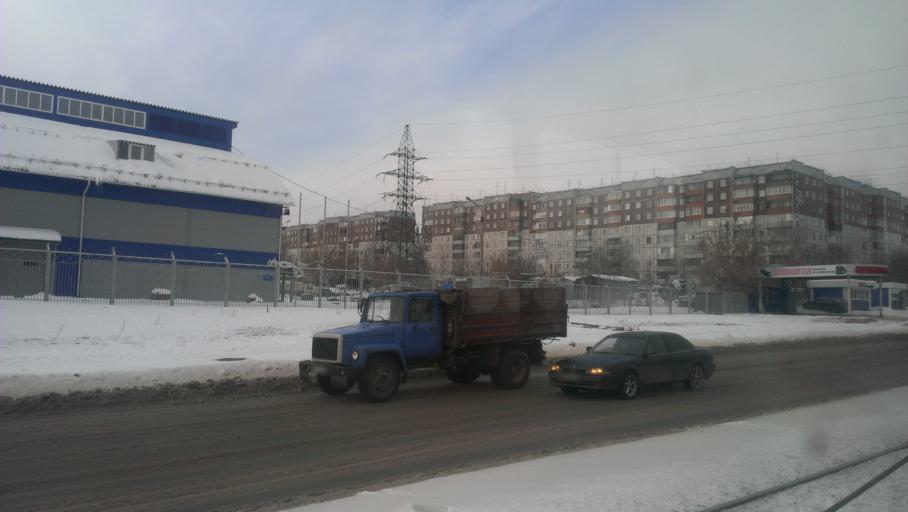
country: RU
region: Altai Krai
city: Novosilikatnyy
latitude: 53.3546
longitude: 83.6736
